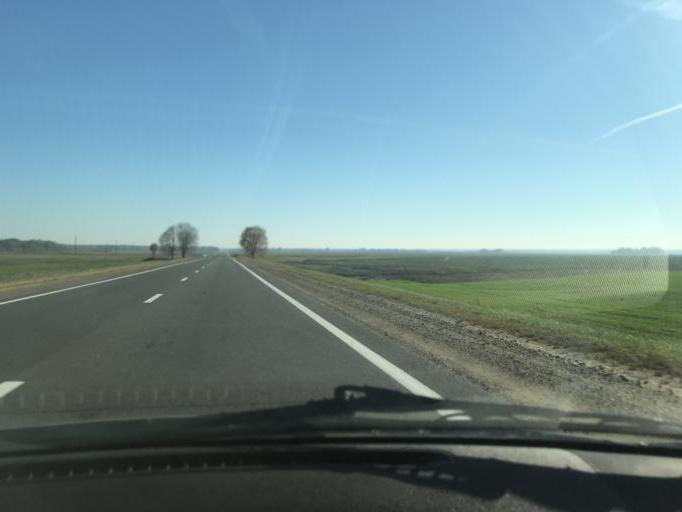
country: BY
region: Brest
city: Ivanava
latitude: 52.1561
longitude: 25.6607
